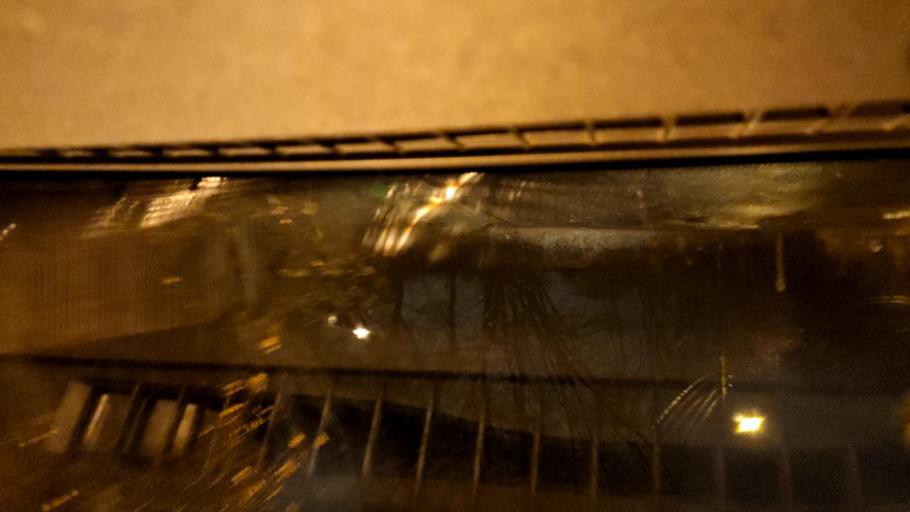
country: RU
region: Perm
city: Perm
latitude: 58.0236
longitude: 56.2801
